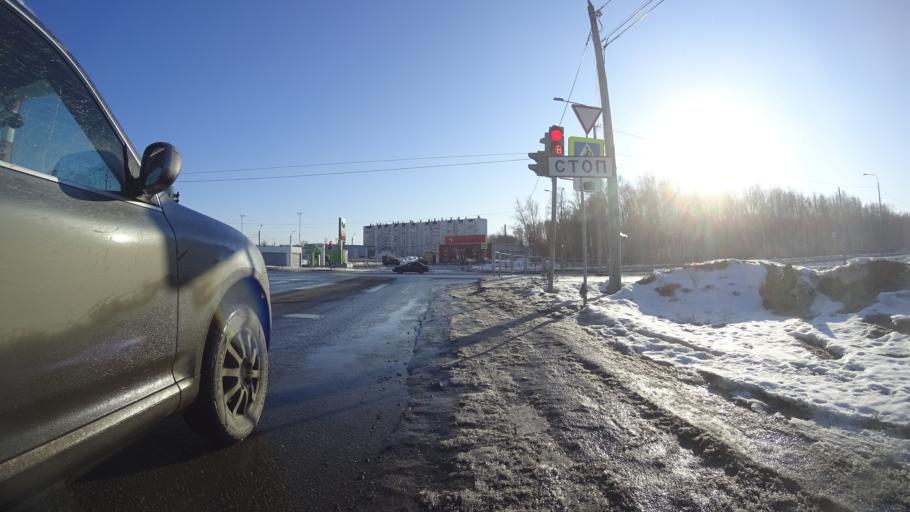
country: RU
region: Chelyabinsk
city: Roshchino
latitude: 55.2087
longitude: 61.3168
